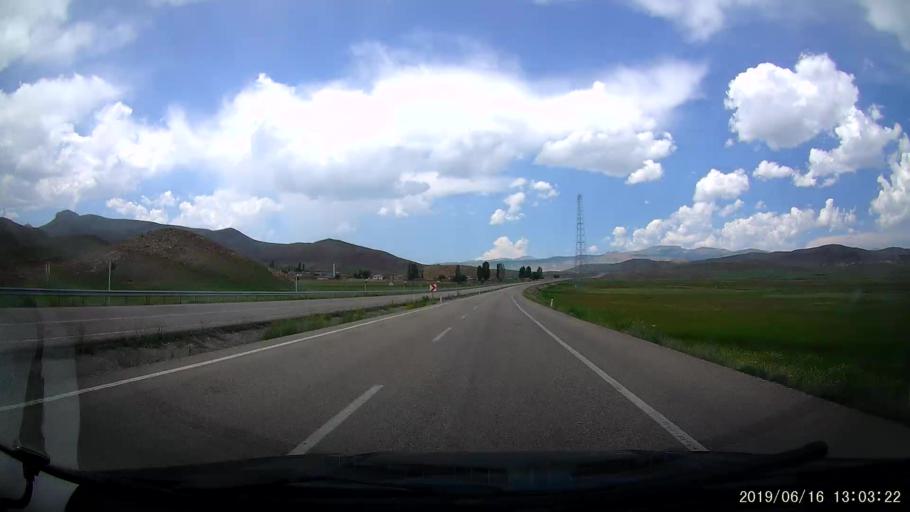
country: TR
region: Agri
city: Sulucem
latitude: 39.5808
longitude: 43.7915
